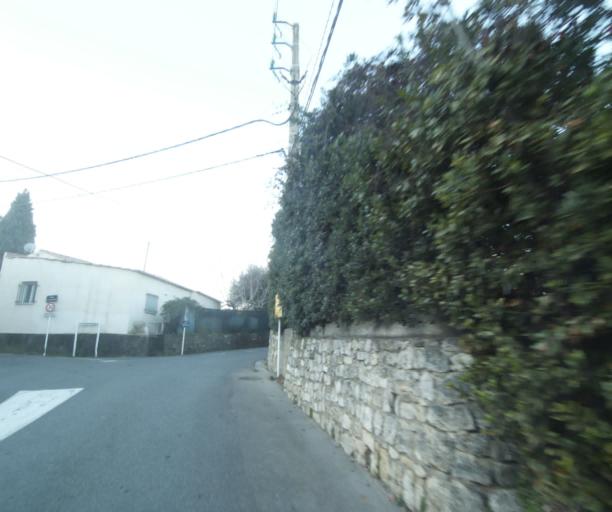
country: FR
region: Provence-Alpes-Cote d'Azur
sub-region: Departement des Alpes-Maritimes
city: Vallauris
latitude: 43.5863
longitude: 7.0809
